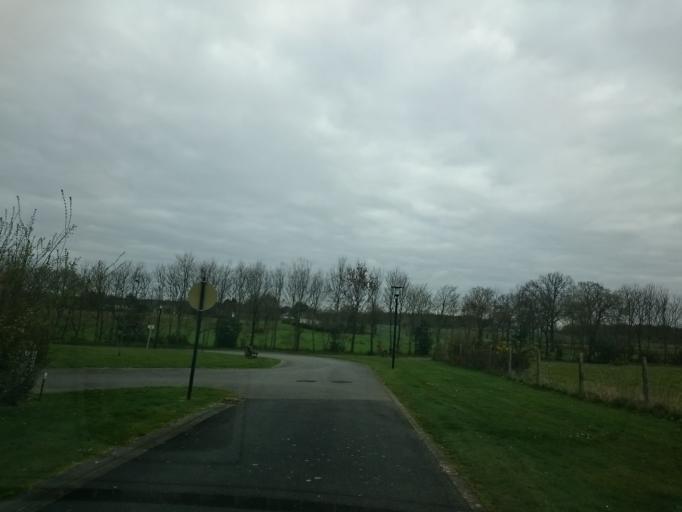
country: FR
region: Brittany
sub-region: Departement d'Ille-et-Vilaine
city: Crevin
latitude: 47.9342
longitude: -1.6476
